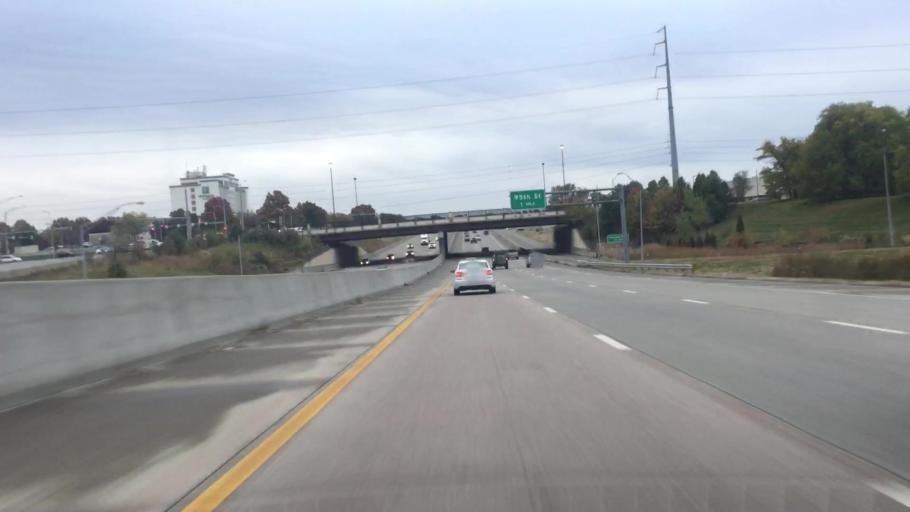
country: US
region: Kansas
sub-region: Johnson County
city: Lenexa
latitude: 38.9725
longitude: -94.7169
